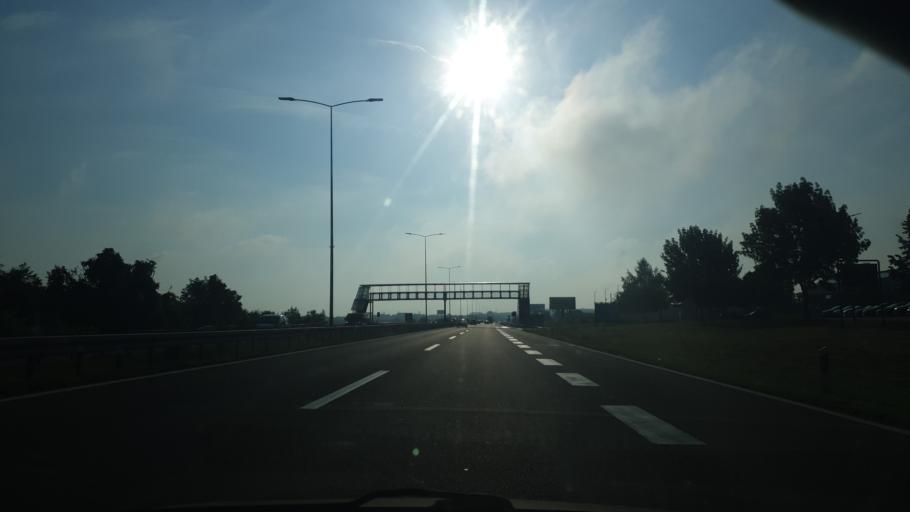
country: RS
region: Central Serbia
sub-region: Belgrade
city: Surcin
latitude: 44.8345
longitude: 20.3093
